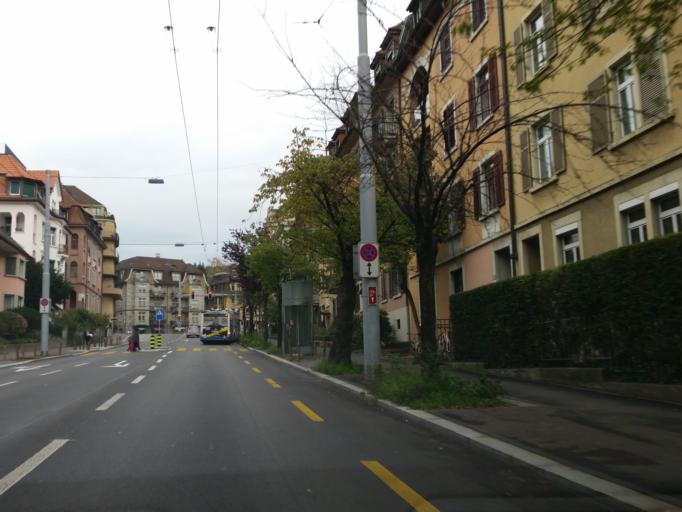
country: CH
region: Zurich
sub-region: Bezirk Zuerich
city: Zuerich (Kreis 6) / Unterstrass
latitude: 47.3913
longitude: 8.5368
